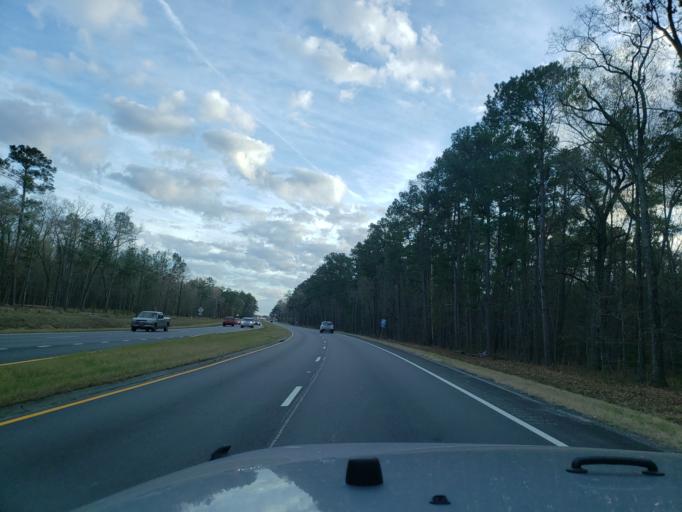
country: US
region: Georgia
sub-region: Chatham County
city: Port Wentworth
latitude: 32.2081
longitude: -81.2012
